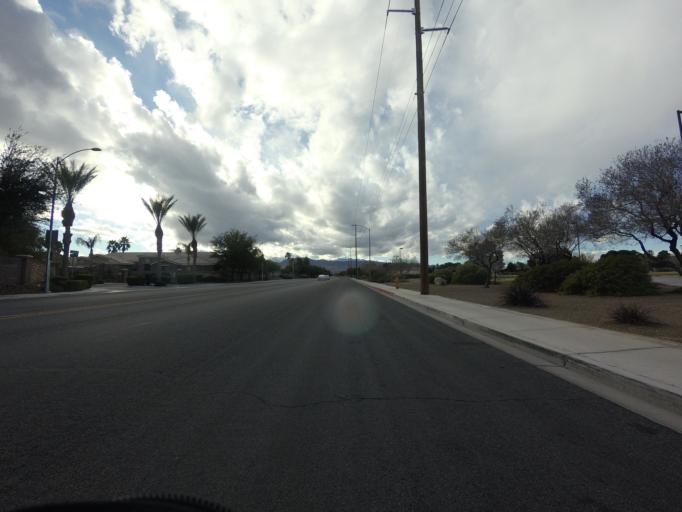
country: US
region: Nevada
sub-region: Clark County
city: Las Vegas
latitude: 36.2694
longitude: -115.2389
